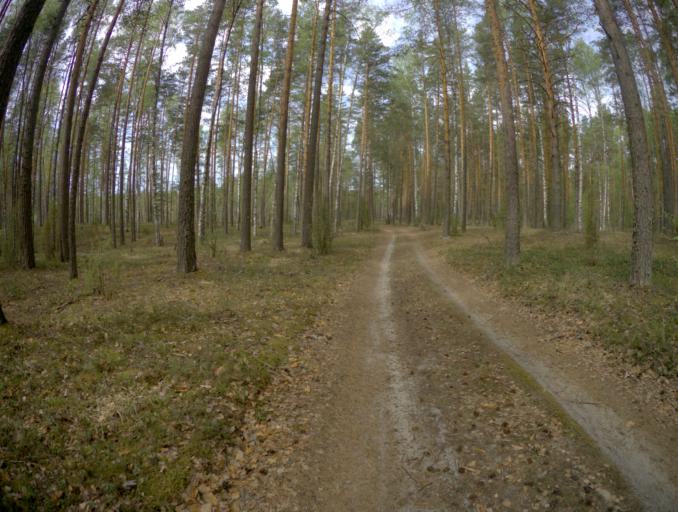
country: RU
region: Ivanovo
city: Talitsy
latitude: 56.4849
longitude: 42.1603
